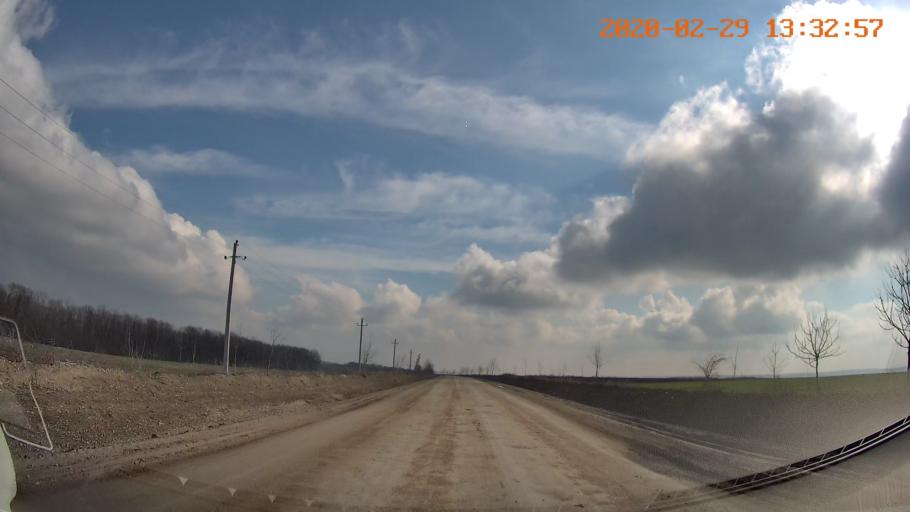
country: MD
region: Telenesti
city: Camenca
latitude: 47.8763
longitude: 28.6130
